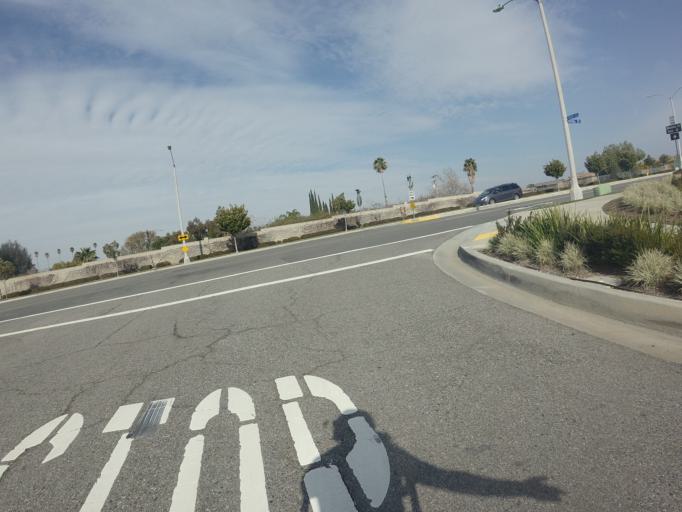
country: US
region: California
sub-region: Riverside County
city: Corona
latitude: 33.8423
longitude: -117.5993
